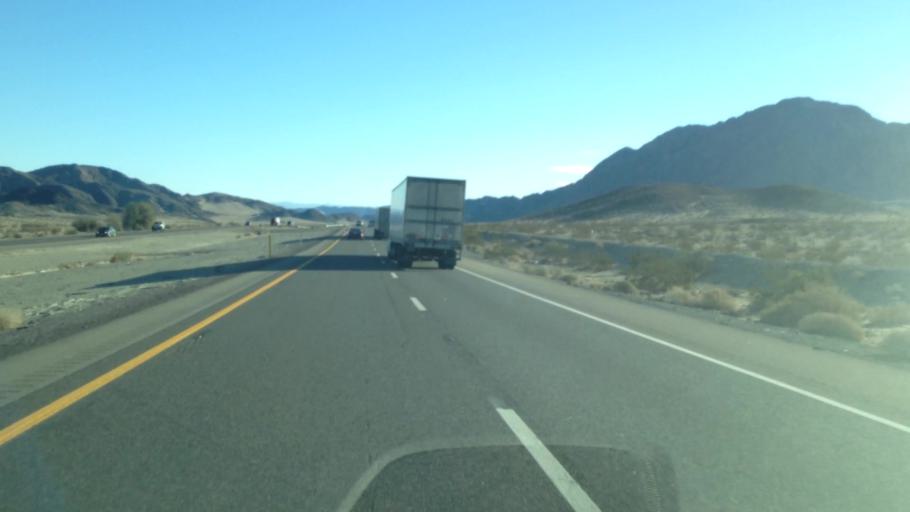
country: US
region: California
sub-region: San Bernardino County
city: Fort Irwin
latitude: 35.0838
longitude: -116.3745
